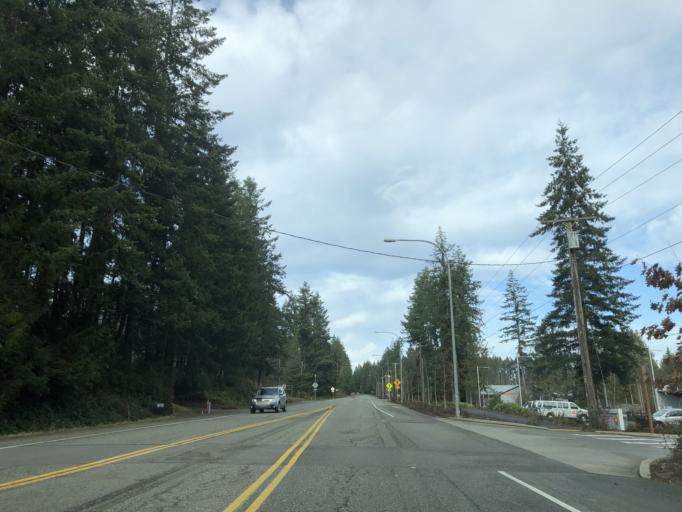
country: US
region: Washington
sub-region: Kitsap County
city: Poulsbo
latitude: 47.7587
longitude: -122.6520
